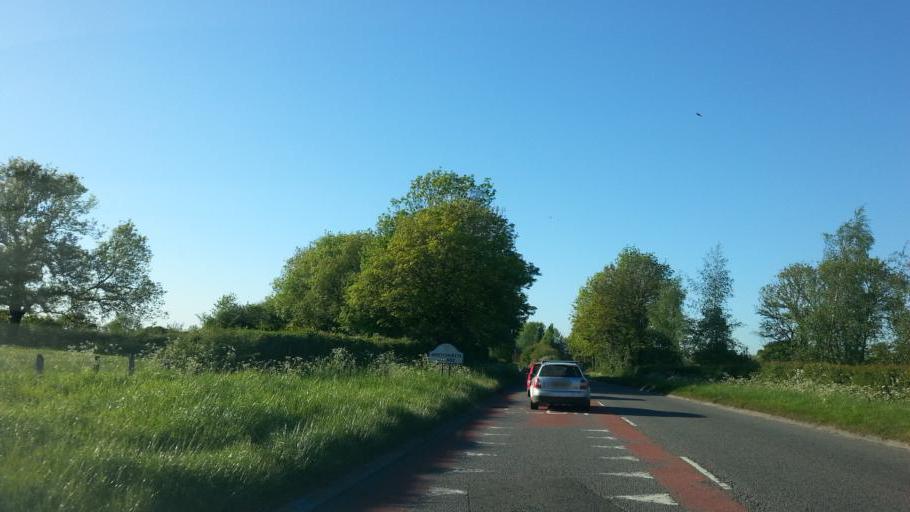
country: GB
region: England
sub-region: Bath and North East Somerset
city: Whitchurch
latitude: 51.3983
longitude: -2.5513
